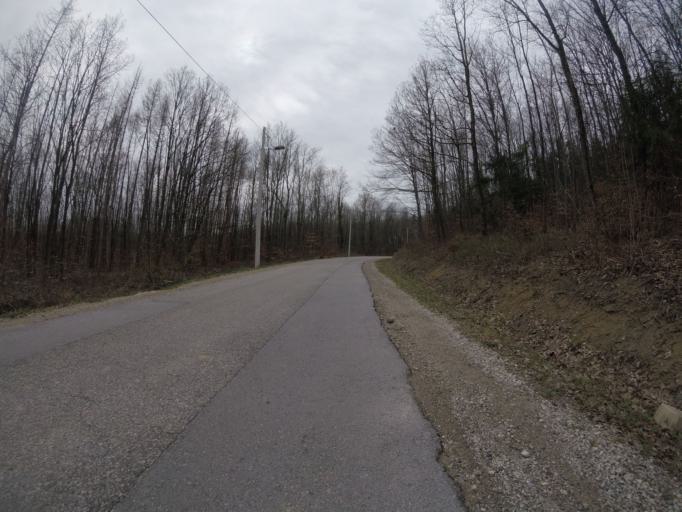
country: HR
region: Grad Zagreb
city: Strmec
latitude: 45.6373
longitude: 15.9342
